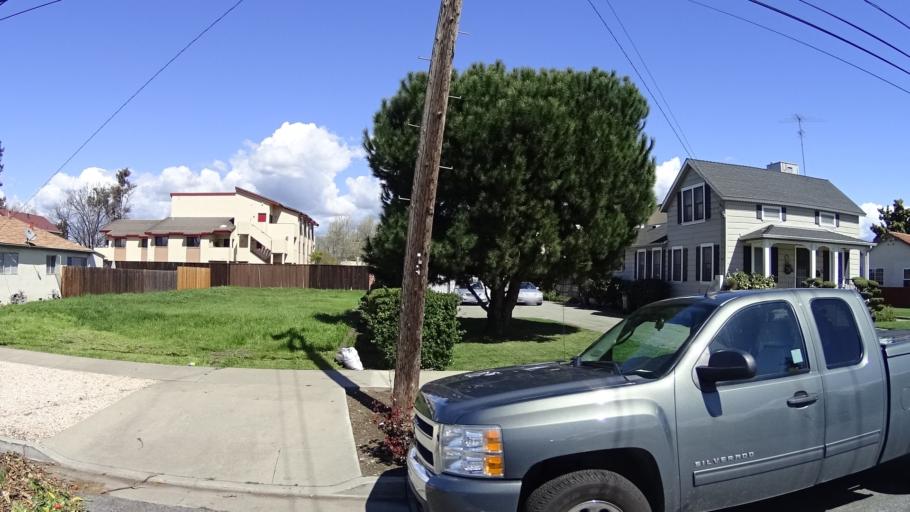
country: US
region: California
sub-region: Santa Clara County
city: San Jose
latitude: 37.3611
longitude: -121.8848
